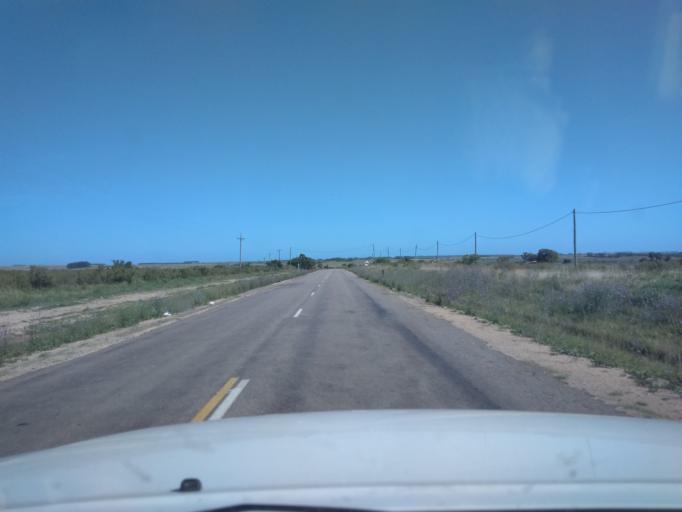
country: UY
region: Canelones
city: San Ramon
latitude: -34.2313
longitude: -55.9285
